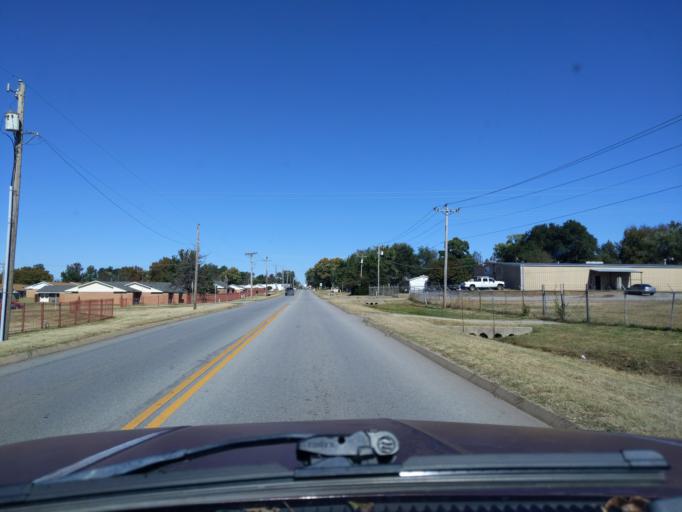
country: US
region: Oklahoma
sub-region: Creek County
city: Bristow
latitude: 35.8213
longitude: -96.3872
